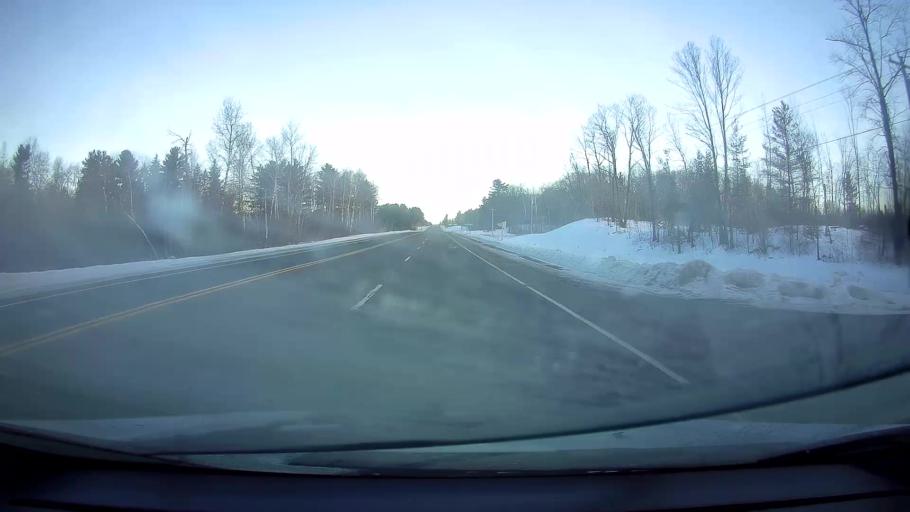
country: US
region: Wisconsin
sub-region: Barron County
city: Cumberland
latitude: 45.5646
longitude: -92.0173
